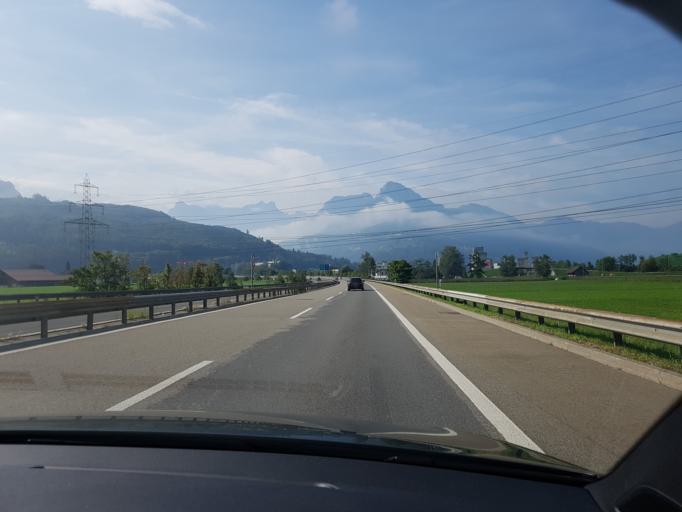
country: CH
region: Schwyz
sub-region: Bezirk Schwyz
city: Ingenbohl
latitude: 47.0103
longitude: 8.6233
